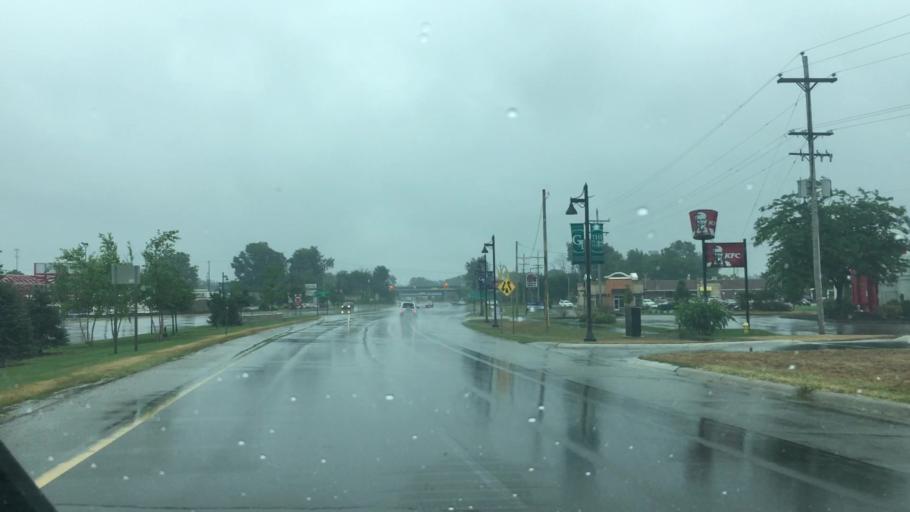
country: US
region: Michigan
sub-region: Ottawa County
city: Jenison
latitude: 42.9039
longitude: -85.7888
